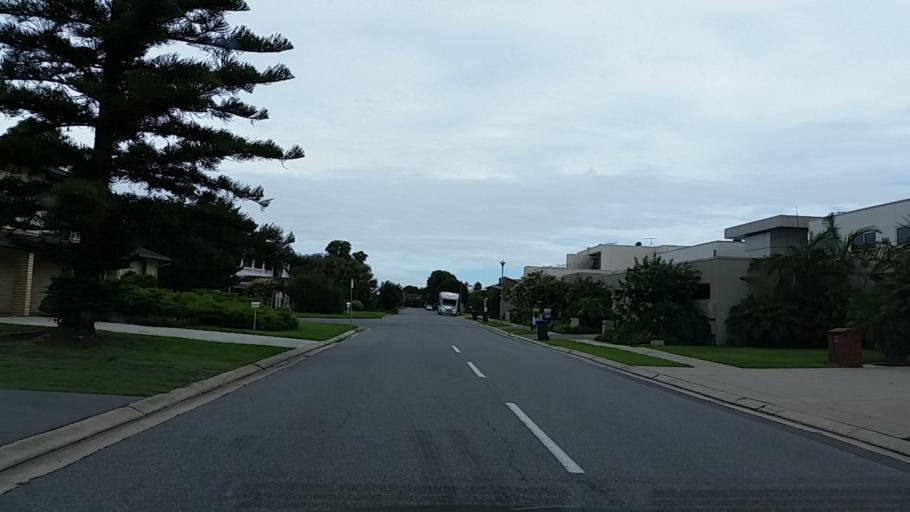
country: AU
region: South Australia
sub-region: Charles Sturt
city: Grange
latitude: -34.8837
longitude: 138.4896
